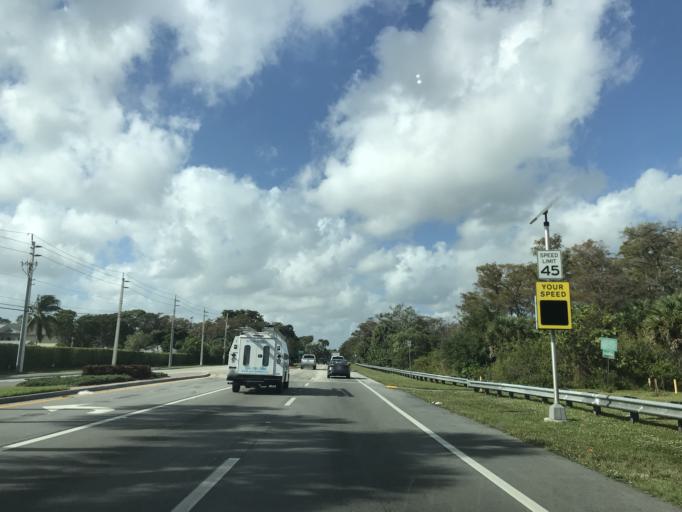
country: US
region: Florida
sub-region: Broward County
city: Coconut Creek
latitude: 26.2599
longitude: -80.1746
